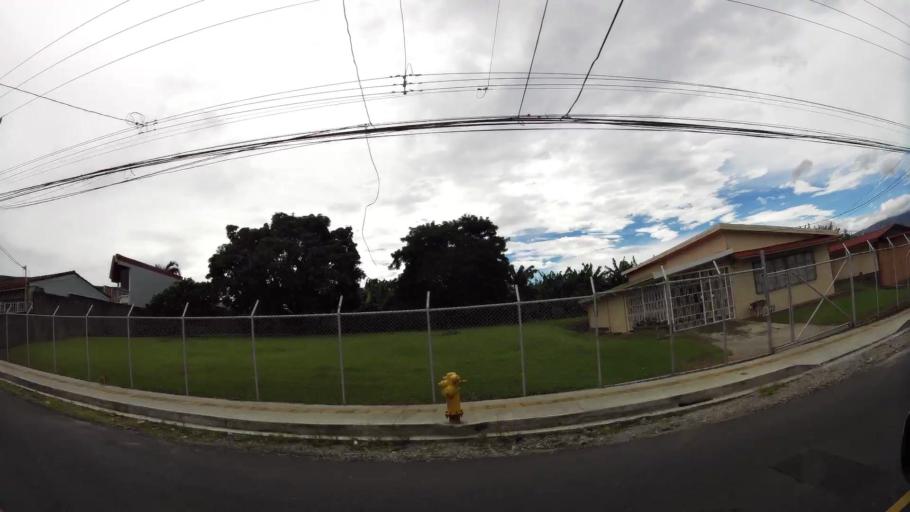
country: CR
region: San Jose
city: Sabanilla
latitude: 9.9441
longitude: -84.0370
